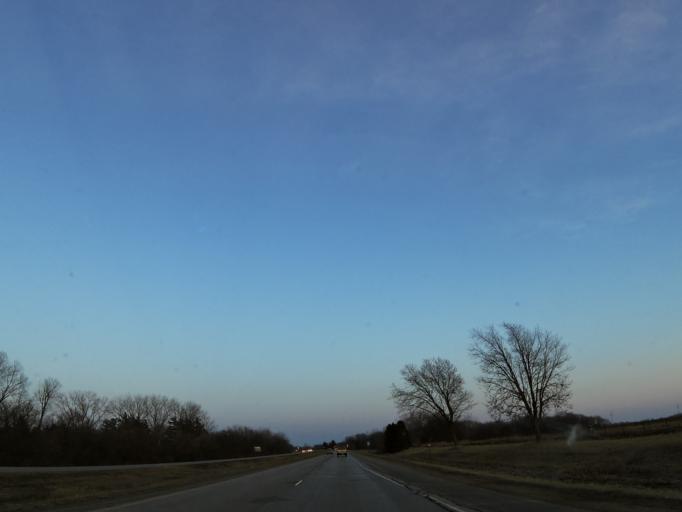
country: US
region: Minnesota
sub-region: Mower County
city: Austin
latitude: 43.6729
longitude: -92.9241
